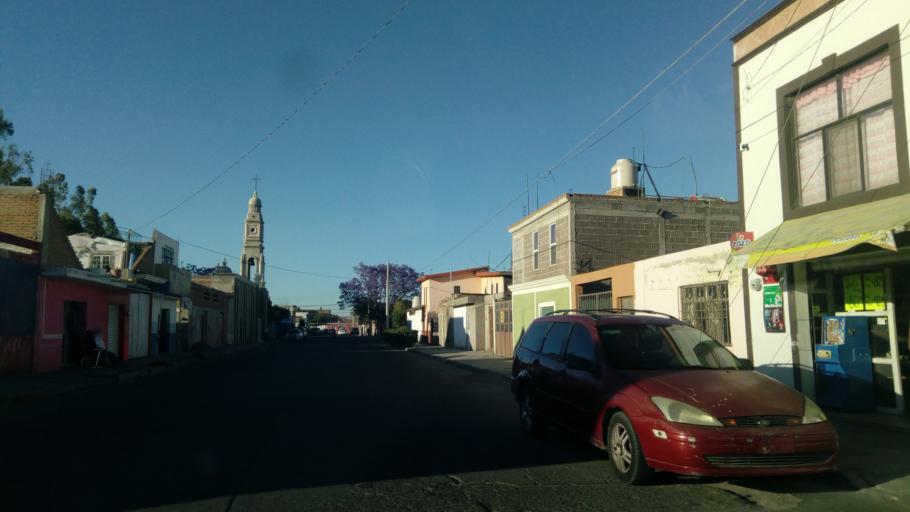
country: MX
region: Durango
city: Victoria de Durango
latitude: 23.9999
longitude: -104.6748
